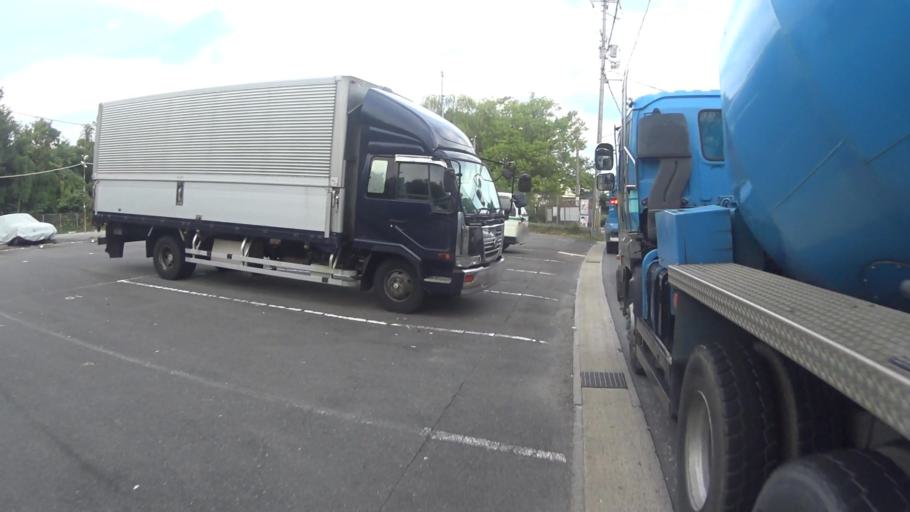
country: JP
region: Kyoto
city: Muko
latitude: 34.9531
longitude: 135.6887
